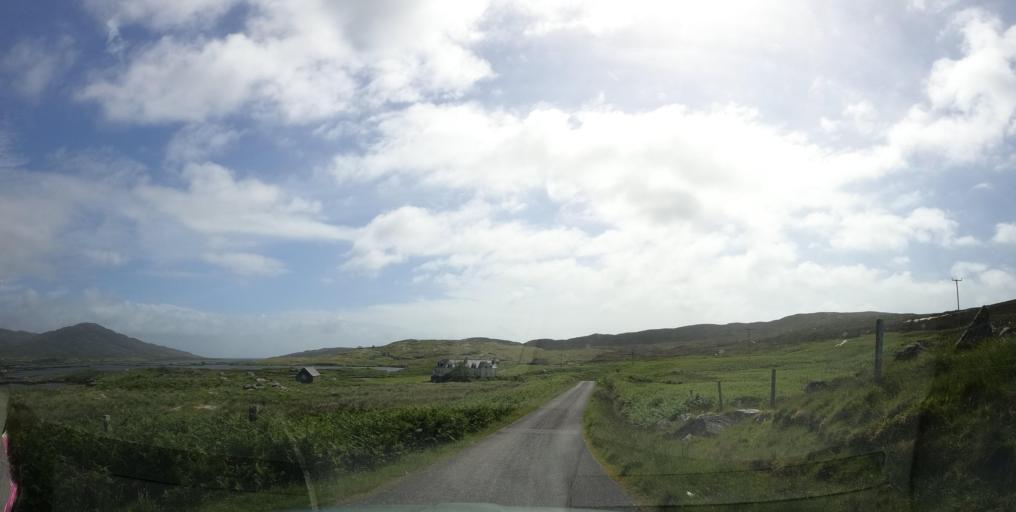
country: GB
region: Scotland
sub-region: Eilean Siar
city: Isle of South Uist
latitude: 57.1372
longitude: -7.3409
